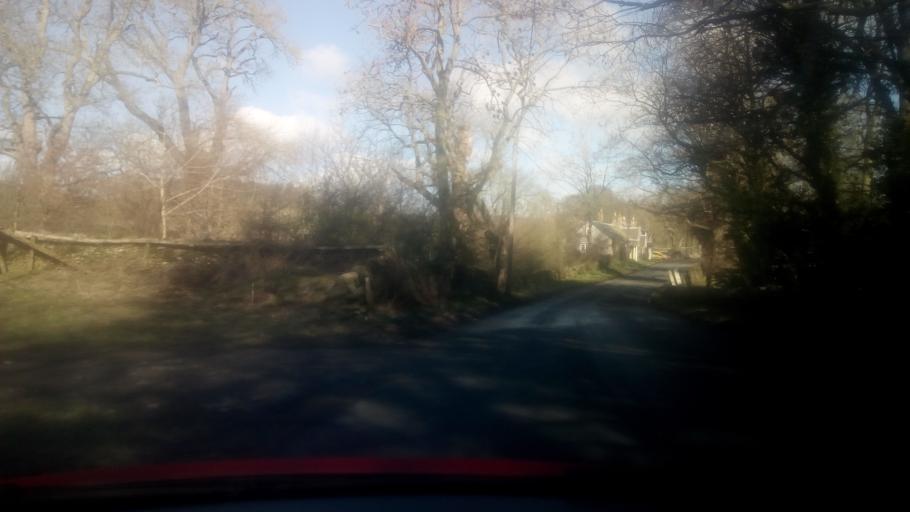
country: GB
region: Scotland
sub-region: The Scottish Borders
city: Selkirk
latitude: 55.5675
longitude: -2.8375
